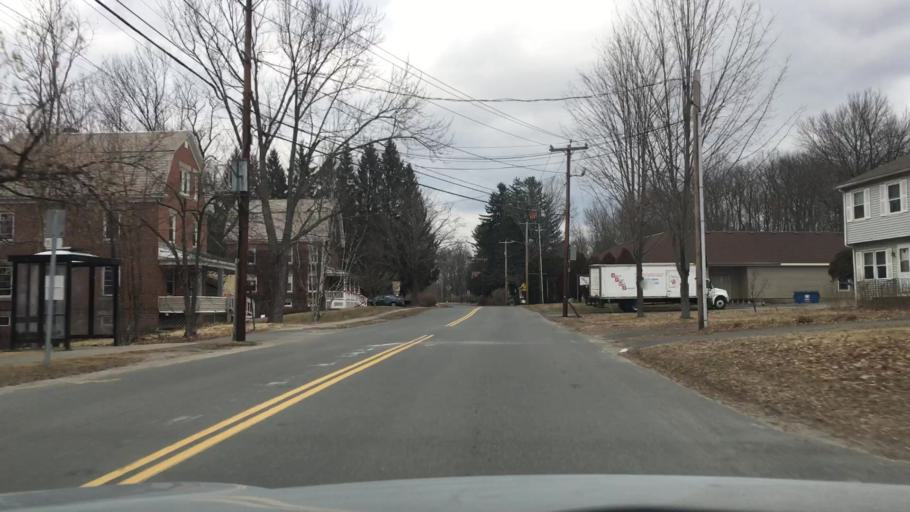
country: US
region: Massachusetts
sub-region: Franklin County
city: Greenfield
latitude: 42.5919
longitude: -72.6110
